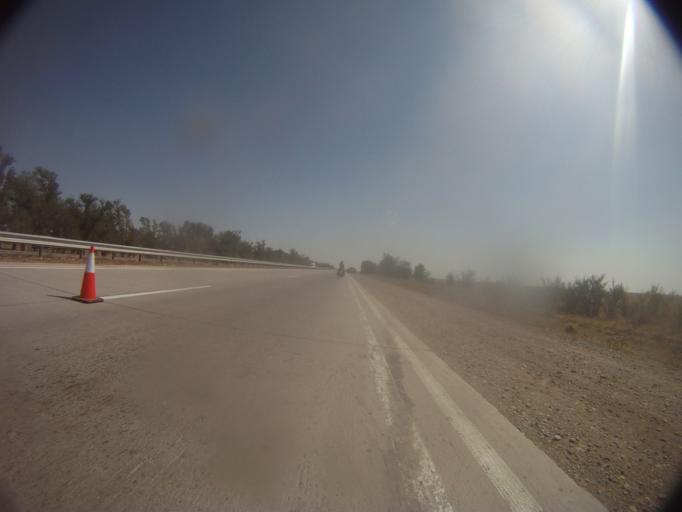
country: KZ
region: Zhambyl
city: Taraz
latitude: 42.7858
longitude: 71.0531
